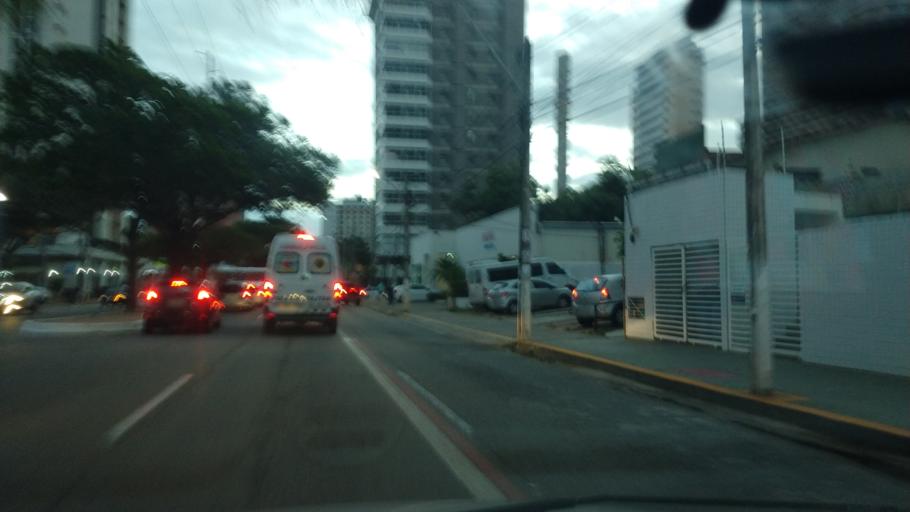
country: BR
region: Rio Grande do Norte
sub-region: Natal
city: Natal
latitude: -5.7865
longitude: -35.2009
